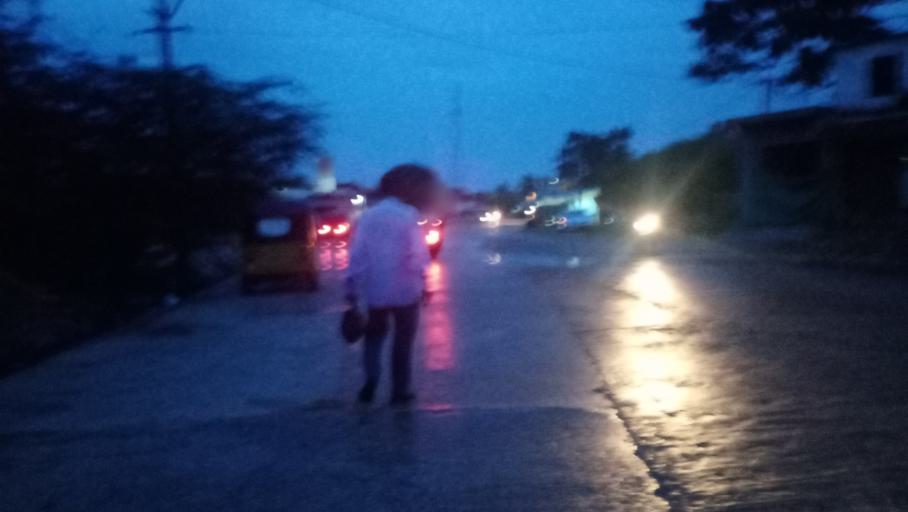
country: IN
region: Karnataka
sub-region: Tumkur
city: Pavagada
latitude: 13.9405
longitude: 77.2763
